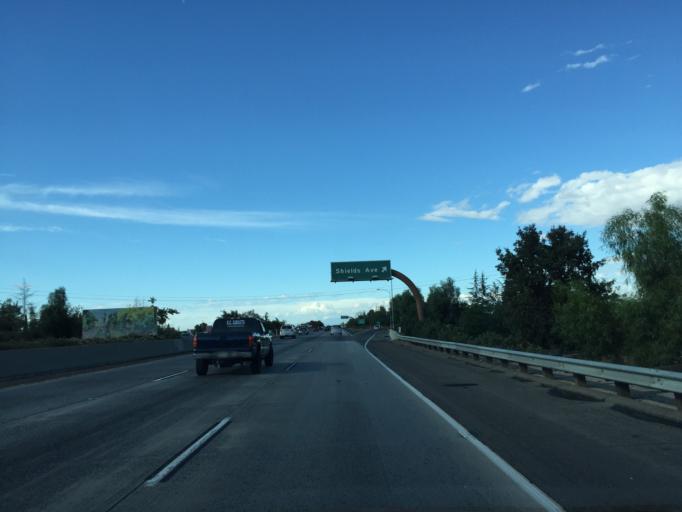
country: US
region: California
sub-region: Fresno County
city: Fresno
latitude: 36.7752
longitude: -119.7848
